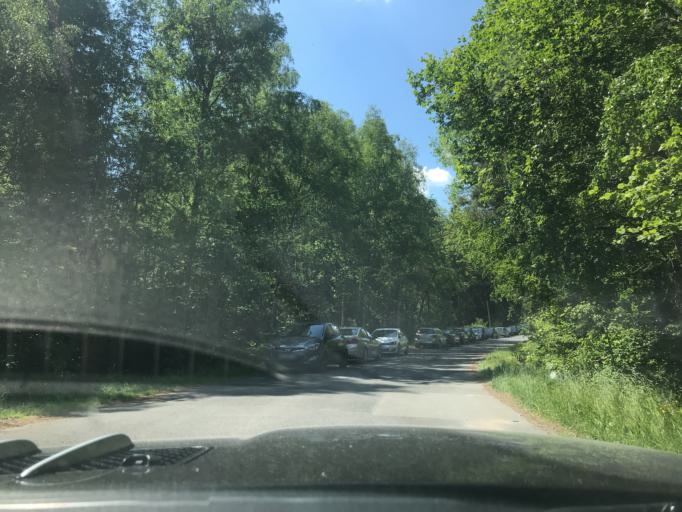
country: DE
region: Thuringia
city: Neuhaus
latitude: 50.7408
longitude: 10.9555
